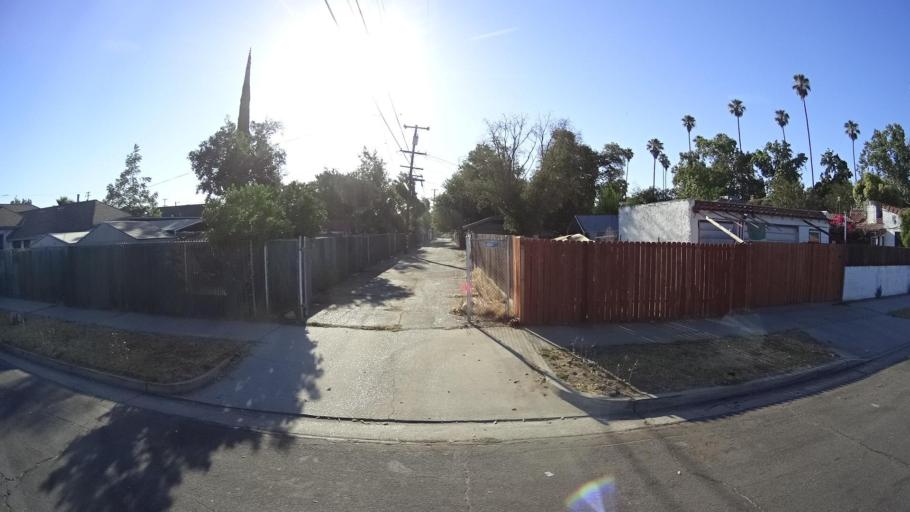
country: US
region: California
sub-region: Fresno County
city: Fresno
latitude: 36.7424
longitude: -119.7644
